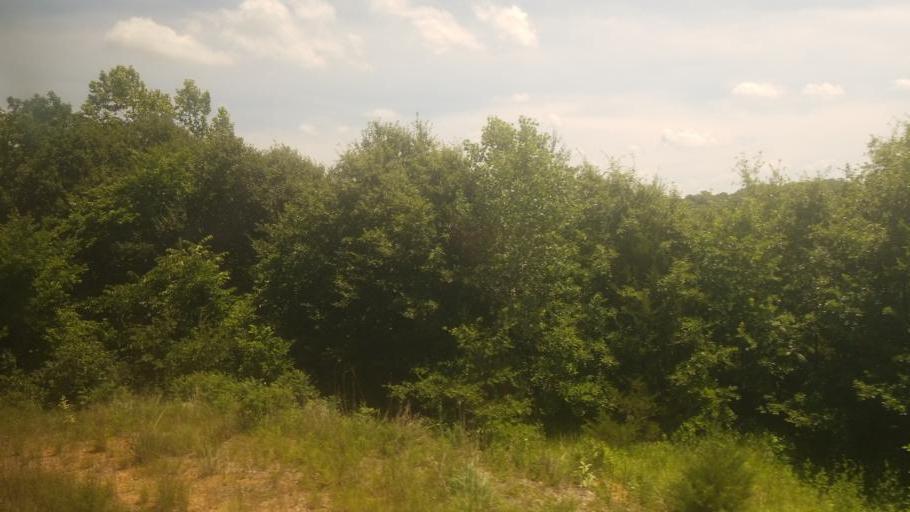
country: US
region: Missouri
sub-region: Linn County
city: Marceline
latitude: 39.8287
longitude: -92.8265
